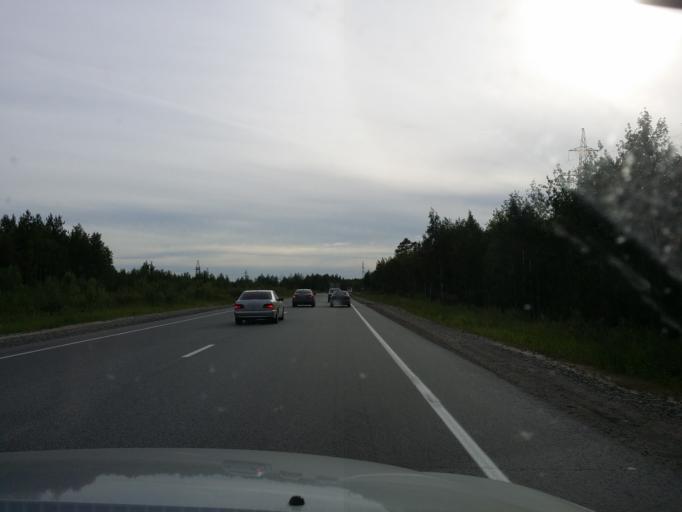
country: RU
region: Khanty-Mansiyskiy Avtonomnyy Okrug
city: Nizhnevartovsk
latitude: 60.9685
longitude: 76.6856
